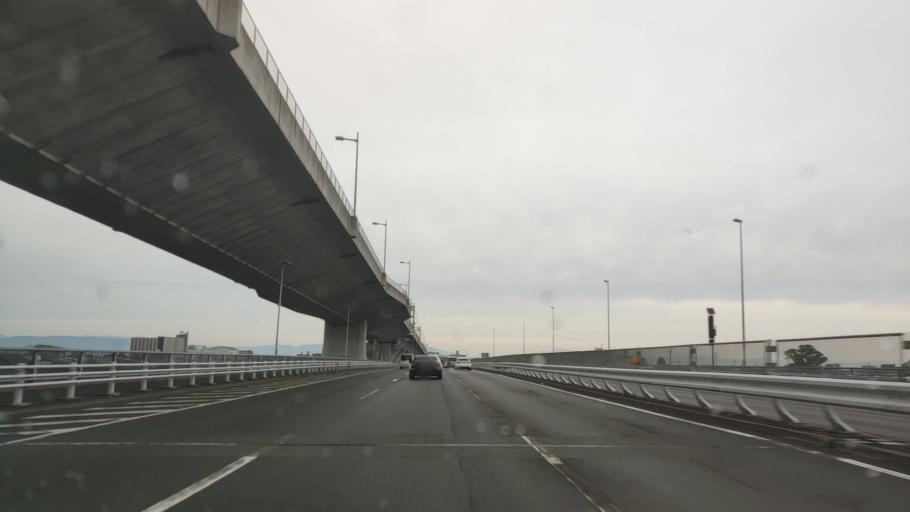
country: JP
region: Aichi
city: Nagoya-shi
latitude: 35.2036
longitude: 136.8772
